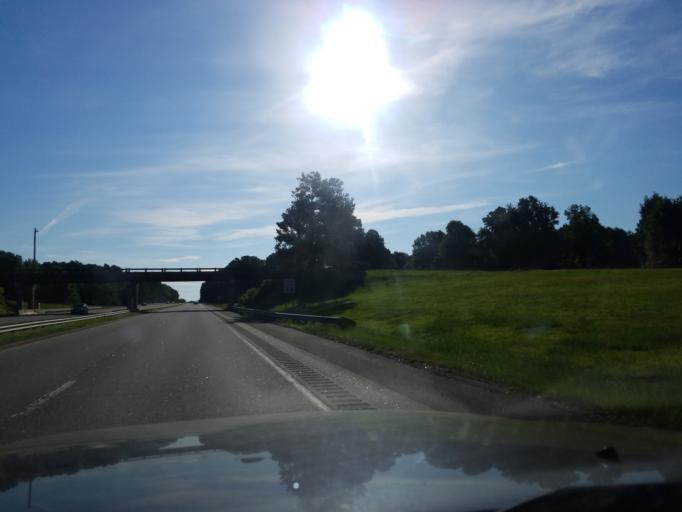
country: US
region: North Carolina
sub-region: Durham County
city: Gorman
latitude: 36.0314
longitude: -78.8423
